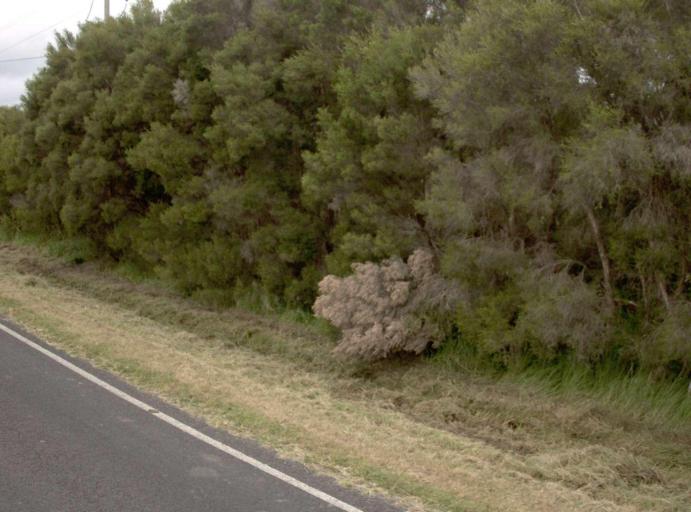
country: AU
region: Victoria
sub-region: Bass Coast
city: North Wonthaggi
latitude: -38.5881
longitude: 145.6159
